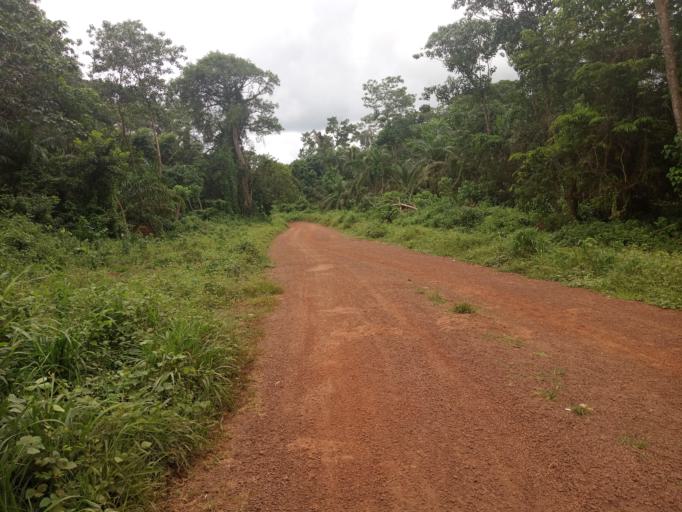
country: SL
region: Northern Province
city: Kamakwie
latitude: 9.5060
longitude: -12.2613
